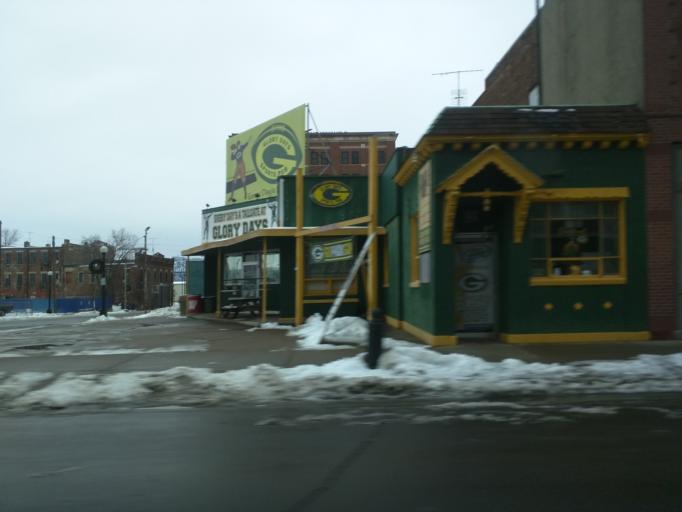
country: US
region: Wisconsin
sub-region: La Crosse County
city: La Crosse
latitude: 43.8102
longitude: -91.2518
